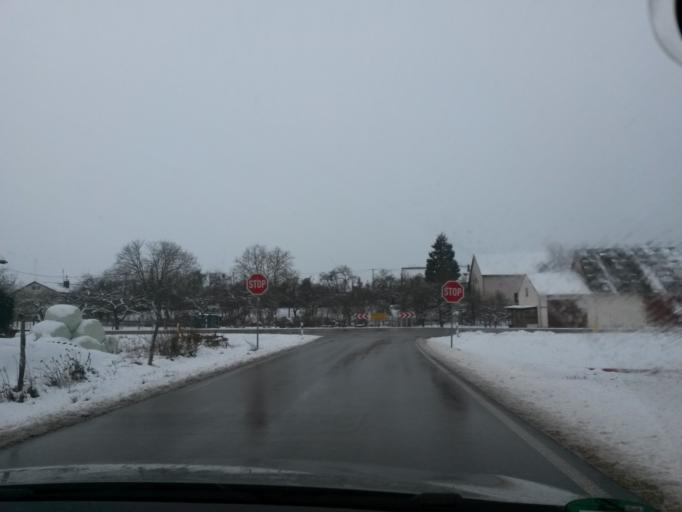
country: DE
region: Baden-Wuerttemberg
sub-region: Regierungsbezirk Stuttgart
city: Bad Uberkingen
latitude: 48.5832
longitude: 9.7664
